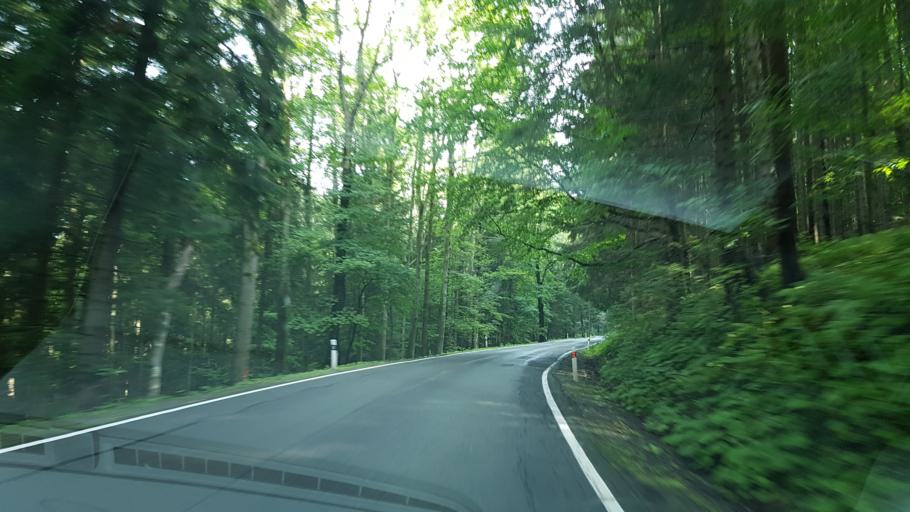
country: CZ
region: Olomoucky
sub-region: Okres Jesenik
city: Jesenik
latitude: 50.2123
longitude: 17.2469
